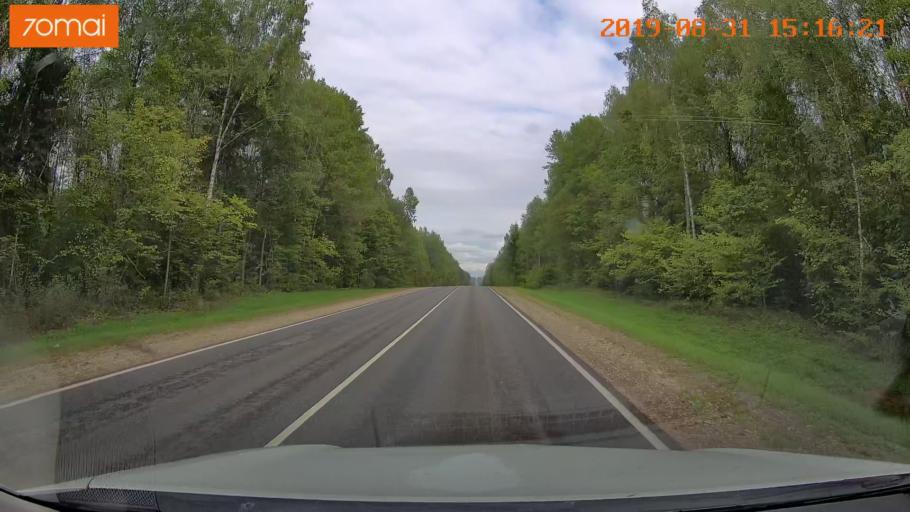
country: RU
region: Kaluga
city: Baryatino
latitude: 54.4591
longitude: 34.3481
